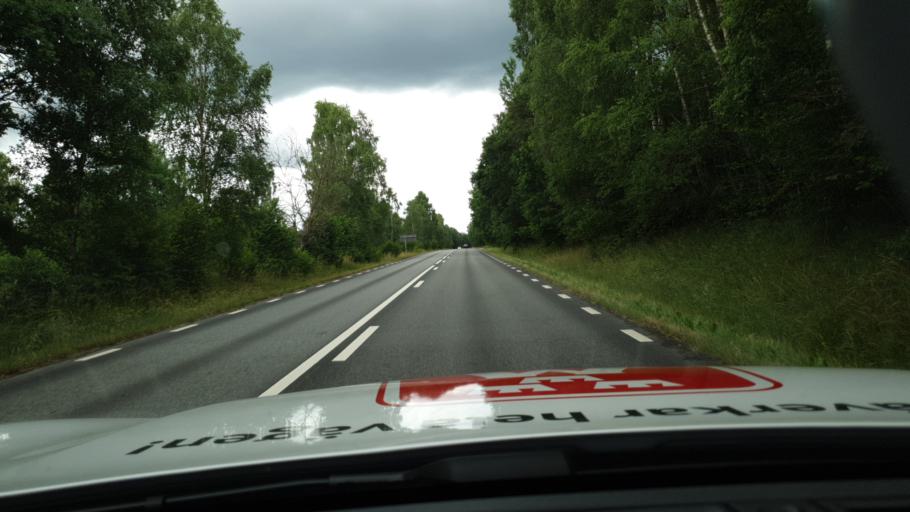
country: SE
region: Skane
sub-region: Hassleholms Kommun
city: Tormestorp
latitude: 56.1100
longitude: 13.7323
